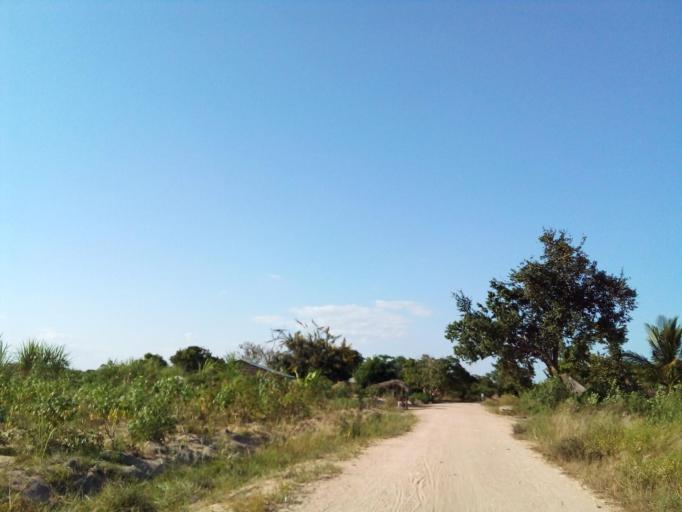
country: MZ
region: Zambezia
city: Quelimane
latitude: -17.5220
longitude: 36.6840
